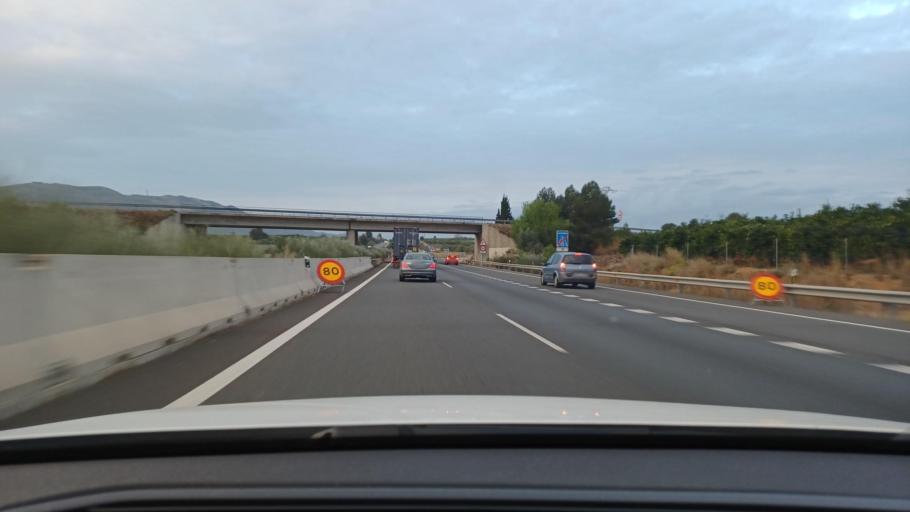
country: ES
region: Valencia
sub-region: Provincia de Valencia
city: Vallada
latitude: 38.9180
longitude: -0.6838
